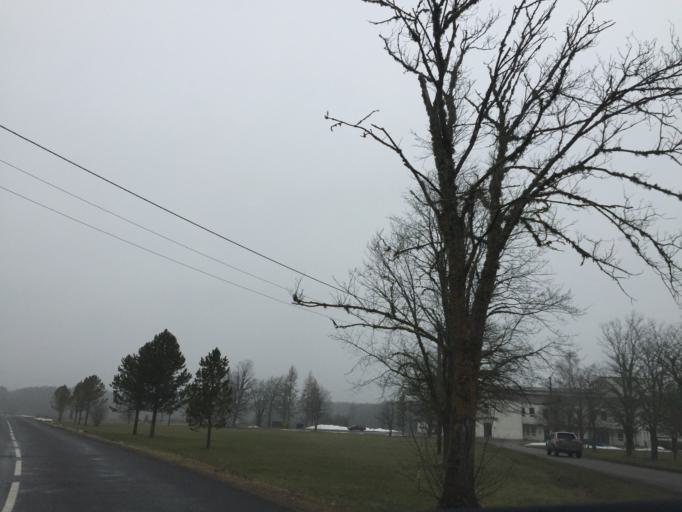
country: EE
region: Saare
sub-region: Kuressaare linn
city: Kuressaare
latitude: 58.3041
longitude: 22.8195
